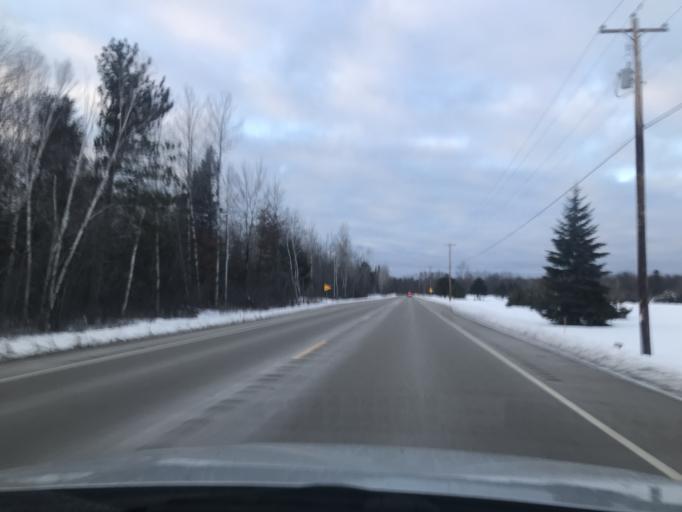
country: US
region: Wisconsin
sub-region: Marinette County
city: Marinette
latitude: 45.1367
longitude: -87.6899
